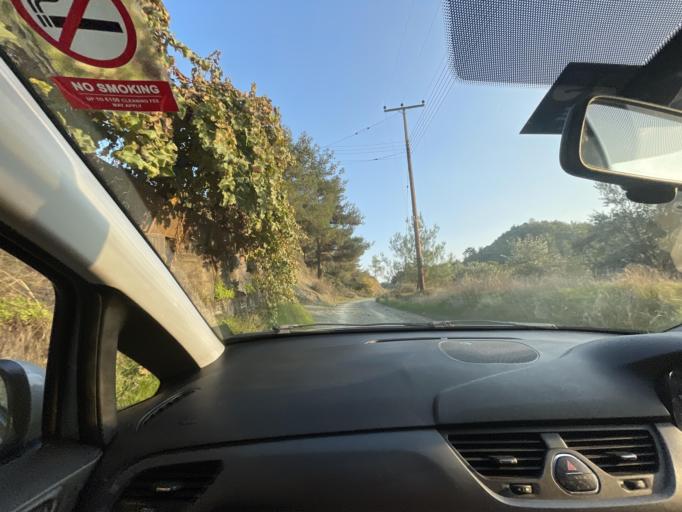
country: CY
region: Limassol
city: Pelendri
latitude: 34.8870
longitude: 32.9732
